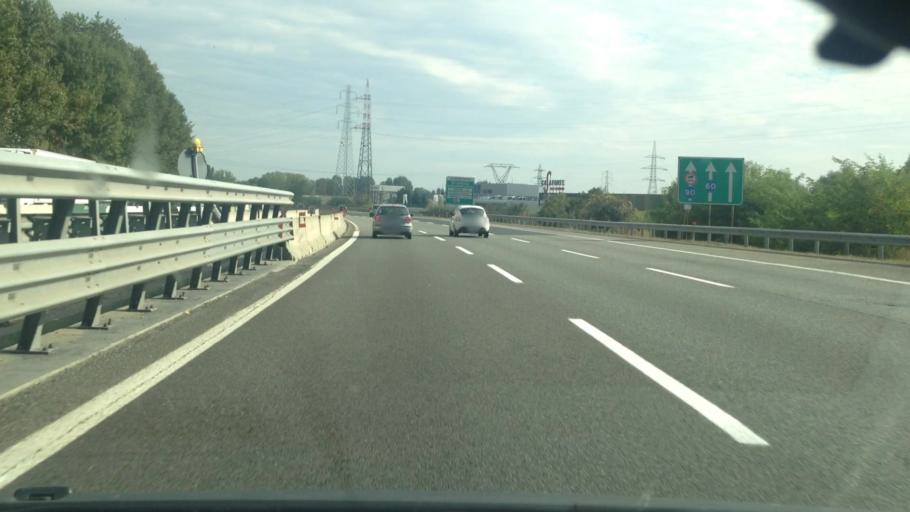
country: IT
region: Piedmont
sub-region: Provincia di Torino
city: Fornaci
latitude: 45.0124
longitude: 7.6045
